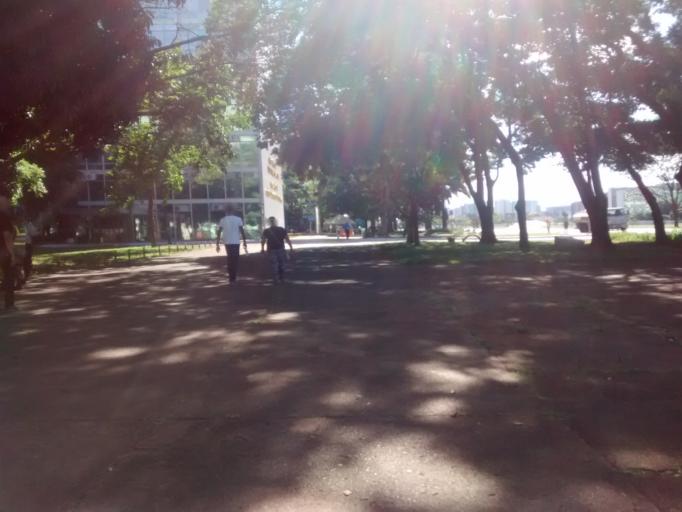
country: BR
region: Federal District
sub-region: Brasilia
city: Brasilia
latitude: -15.7995
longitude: -47.8692
